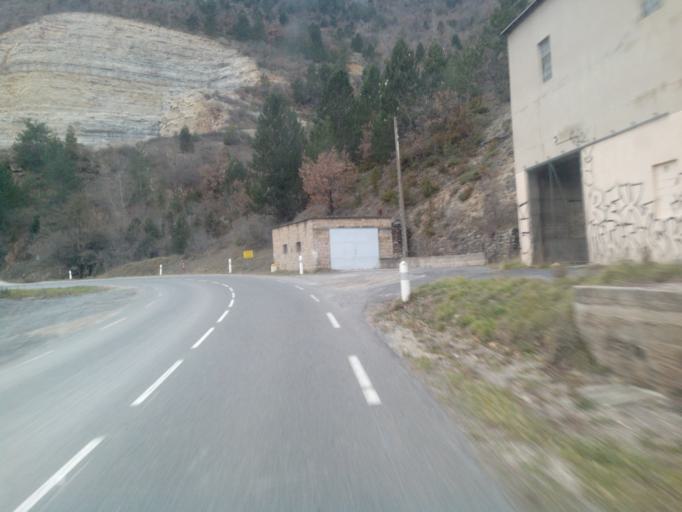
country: FR
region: Languedoc-Roussillon
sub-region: Departement de la Lozere
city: Florac
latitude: 44.2963
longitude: 3.5971
